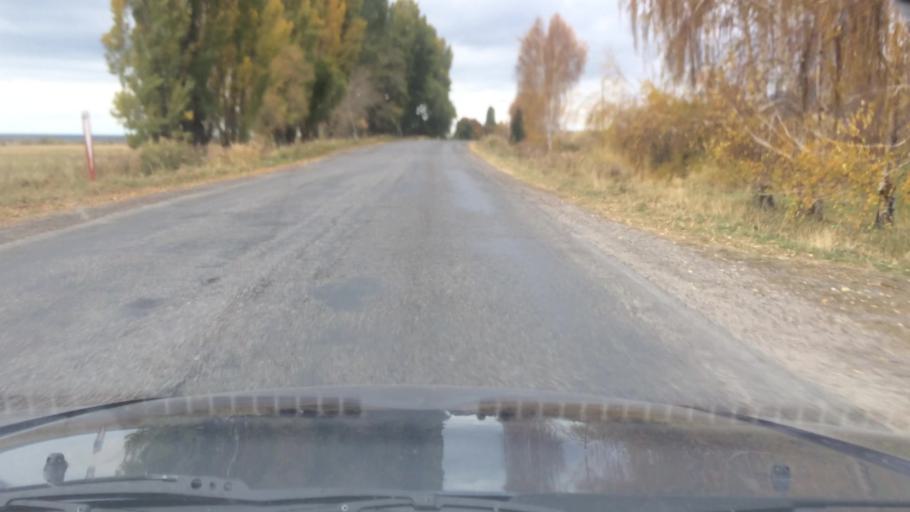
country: KG
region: Ysyk-Koel
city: Tyup
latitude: 42.7633
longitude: 78.1719
